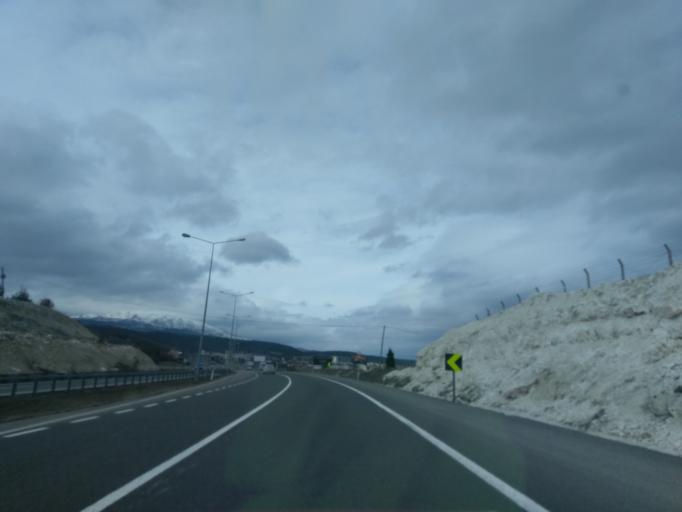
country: TR
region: Kuetahya
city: Kutahya
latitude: 39.3752
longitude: 30.0623
